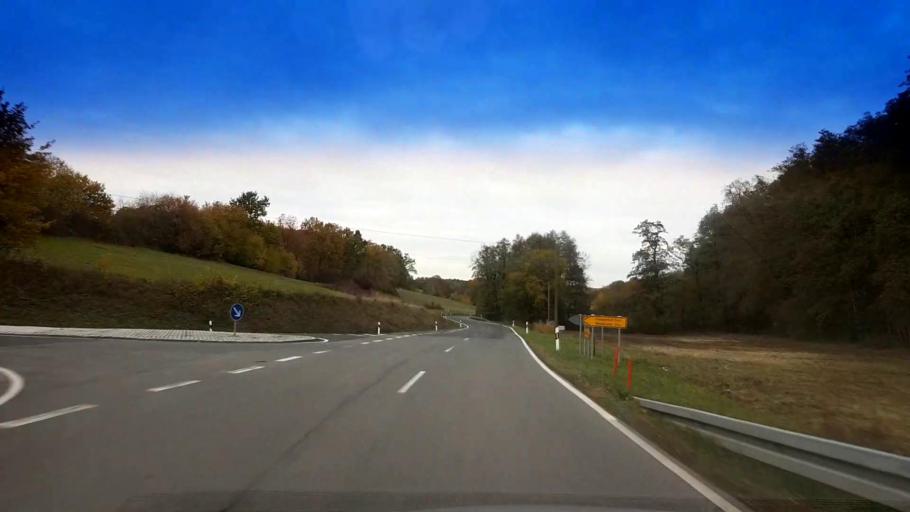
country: DE
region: Bavaria
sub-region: Regierungsbezirk Unterfranken
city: Stettfeld
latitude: 49.9445
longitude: 10.7056
